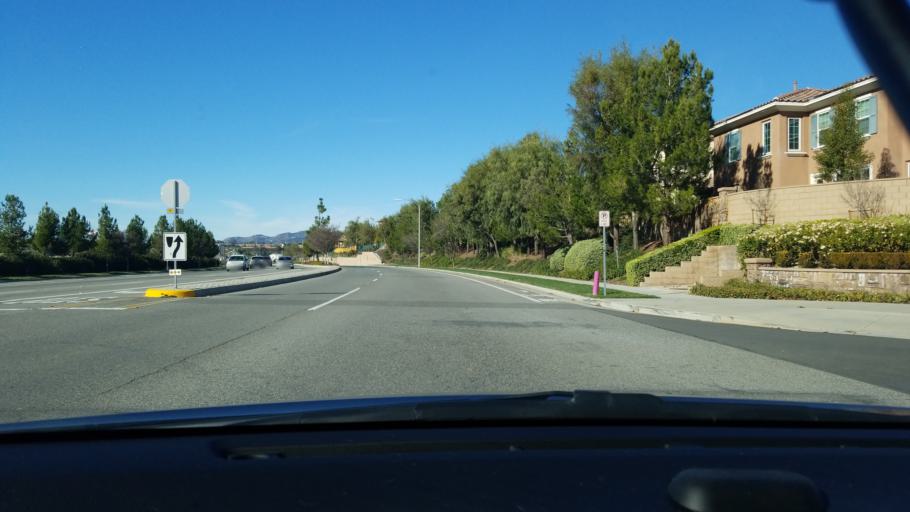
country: US
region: California
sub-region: Riverside County
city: Murrieta Hot Springs
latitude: 33.5379
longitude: -117.1680
